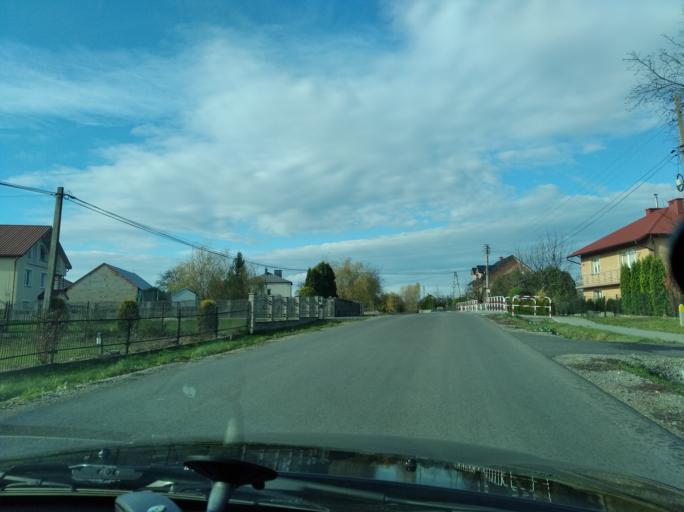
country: PL
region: Subcarpathian Voivodeship
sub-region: Powiat ropczycko-sedziszowski
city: Sedziszow Malopolski
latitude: 50.0771
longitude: 21.7439
